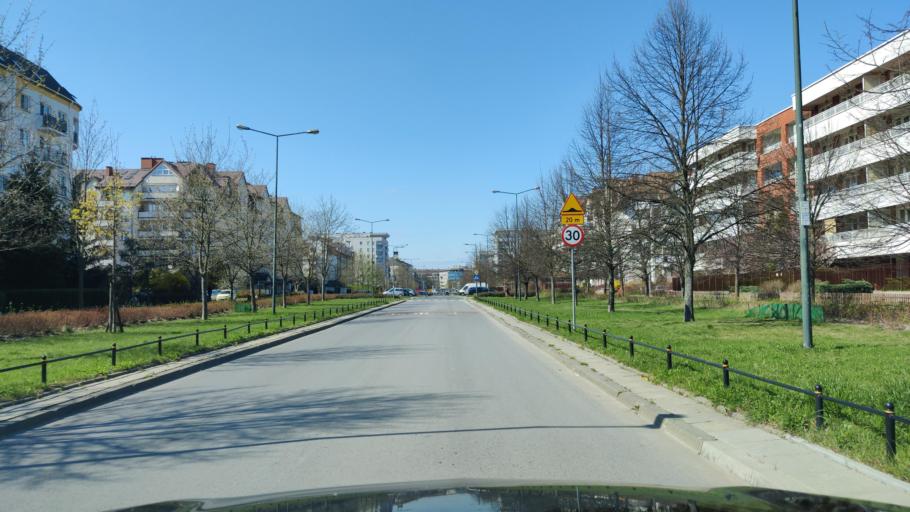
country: PL
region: Masovian Voivodeship
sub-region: Warszawa
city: Kabaty
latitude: 52.1290
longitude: 21.0736
